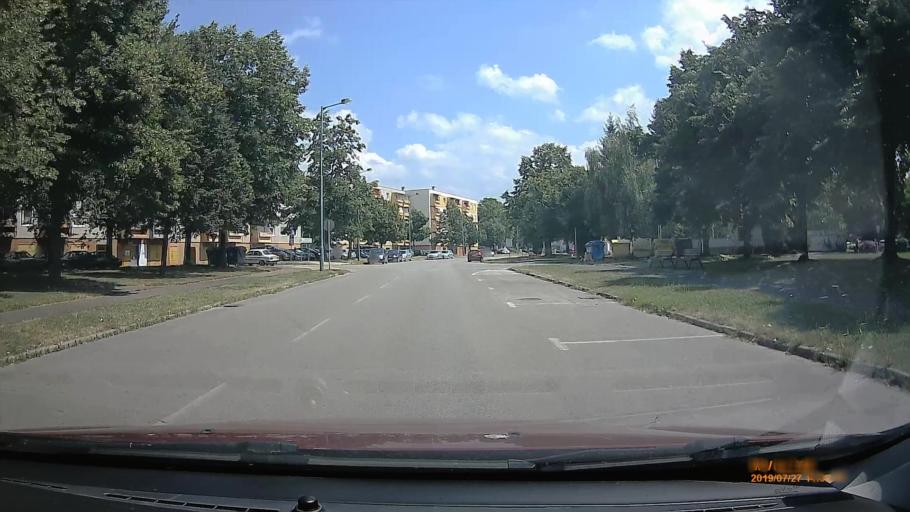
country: HU
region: Veszprem
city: Ajka
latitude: 47.1092
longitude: 17.5654
